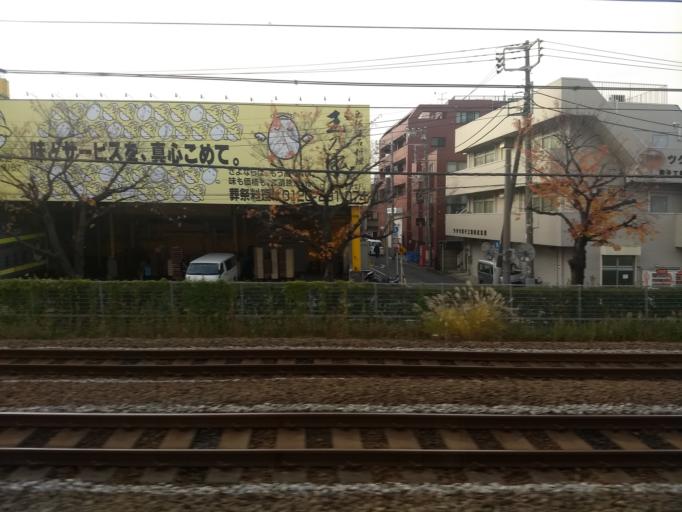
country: JP
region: Kanagawa
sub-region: Kawasaki-shi
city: Kawasaki
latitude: 35.5728
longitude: 139.7203
